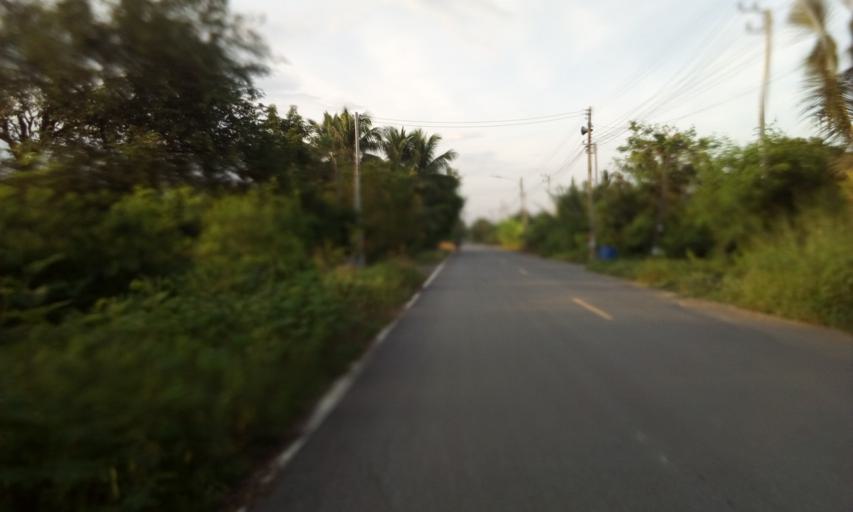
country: TH
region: Pathum Thani
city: Ban Rangsit
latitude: 14.0415
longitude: 100.8476
